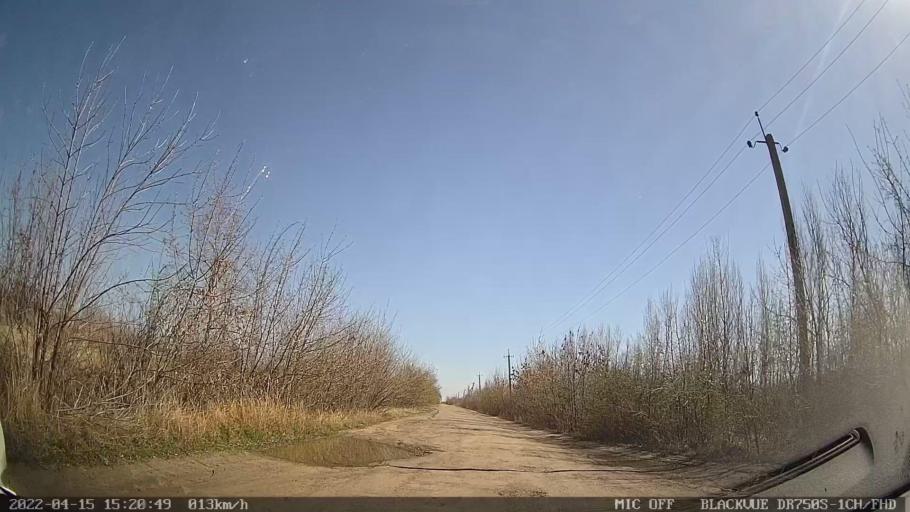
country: MD
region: Raionul Ocnita
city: Otaci
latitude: 48.3851
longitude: 27.9090
